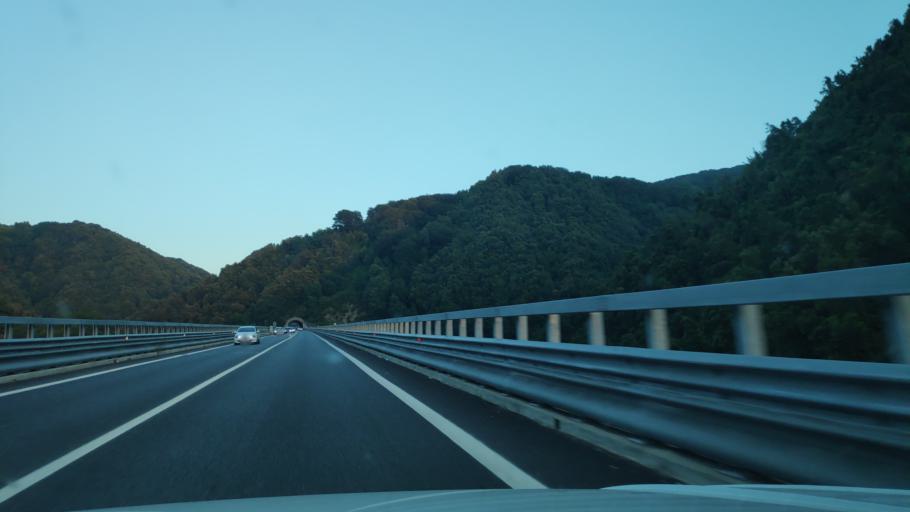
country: IT
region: Calabria
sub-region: Provincia di Reggio Calabria
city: Giffone
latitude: 38.4118
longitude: 16.1404
